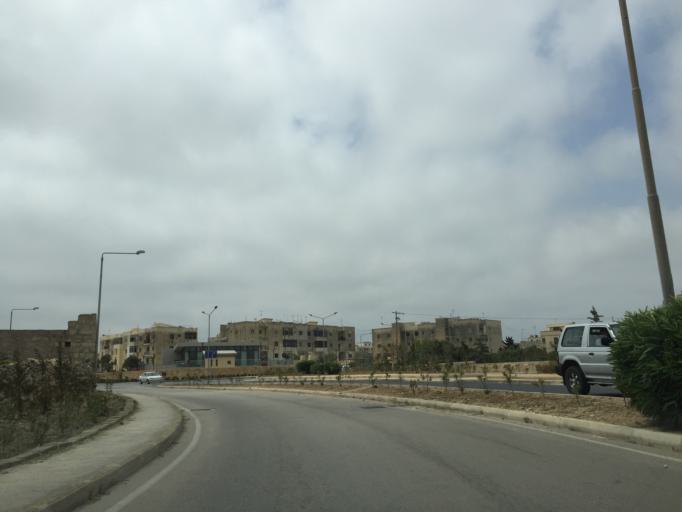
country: MT
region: Ir-Rabat
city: Rabat
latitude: 35.8852
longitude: 14.3908
